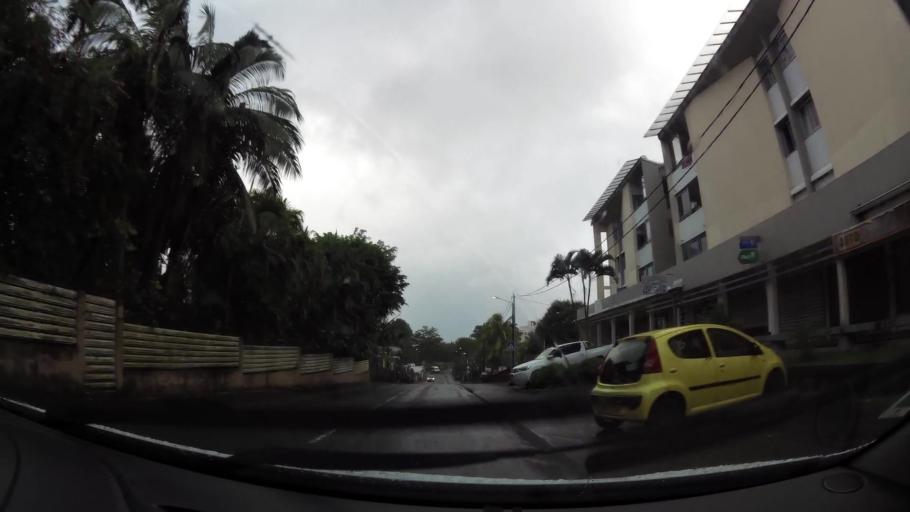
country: RE
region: Reunion
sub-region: Reunion
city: Saint-Benoit
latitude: -21.0374
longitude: 55.7094
